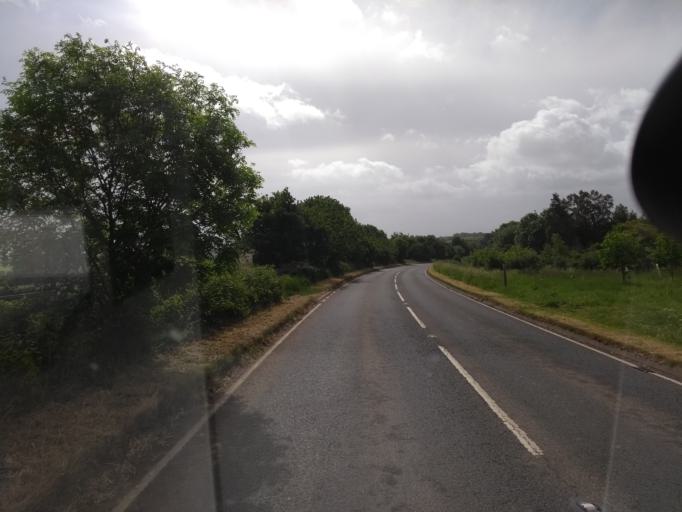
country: GB
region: England
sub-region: Somerset
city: Bishops Lydeard
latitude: 51.1532
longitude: -3.1565
